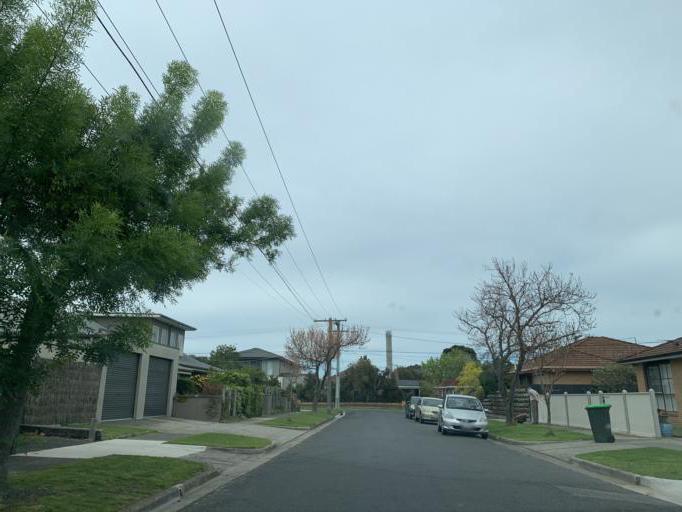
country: AU
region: Victoria
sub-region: Bayside
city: Highett
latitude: -37.9519
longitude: 145.0380
